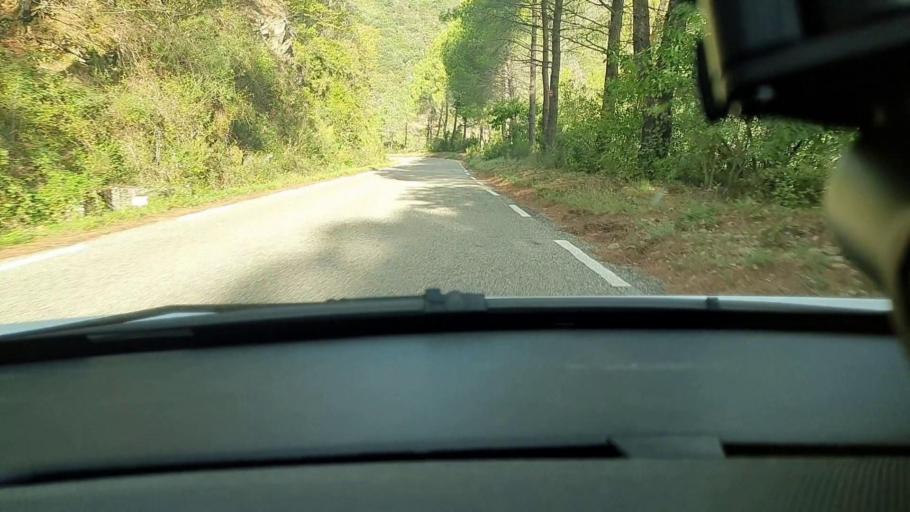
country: FR
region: Languedoc-Roussillon
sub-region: Departement du Gard
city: Besseges
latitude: 44.3168
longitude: 4.0418
